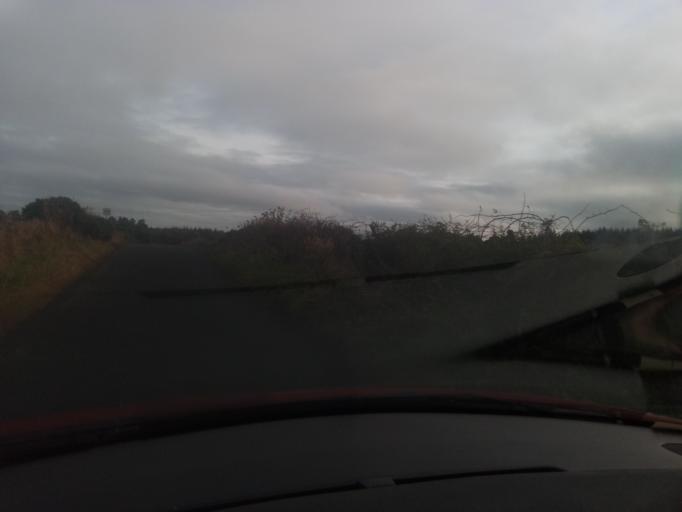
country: GB
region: Scotland
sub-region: The Scottish Borders
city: Jedburgh
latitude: 55.4828
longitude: -2.5805
